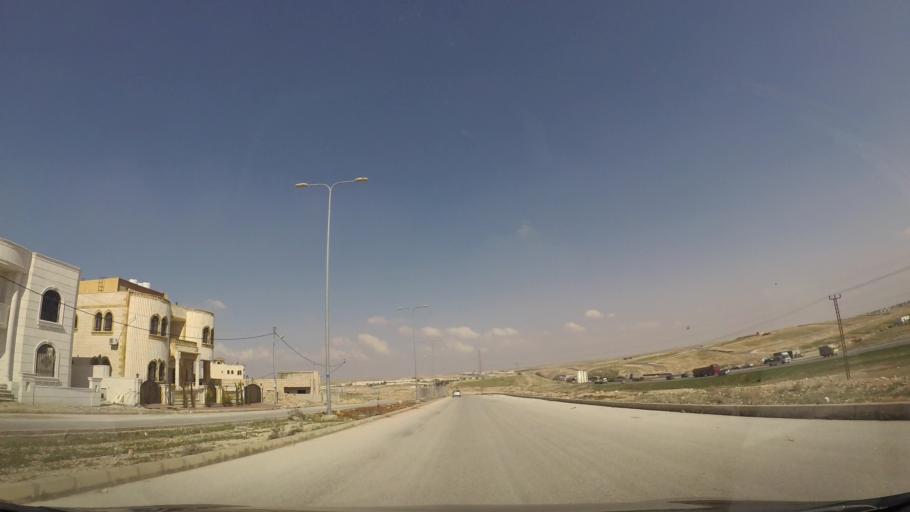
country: JO
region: Zarqa
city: Zarqa
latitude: 32.0480
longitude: 36.1212
